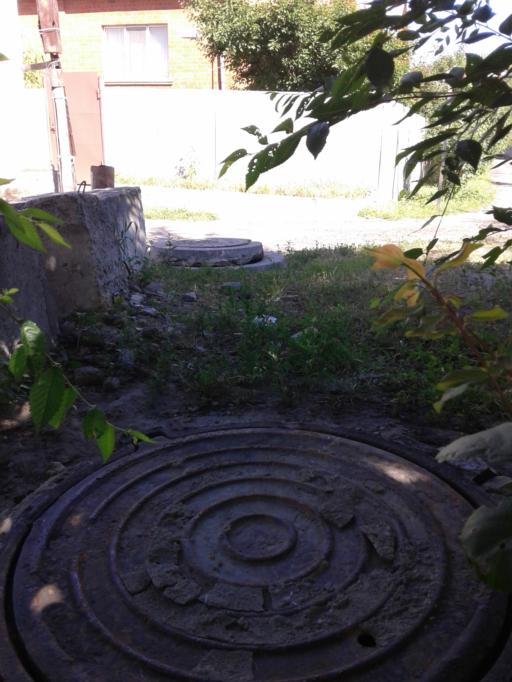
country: RU
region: Voronezj
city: Pridonskoy
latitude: 51.6617
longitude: 39.1191
